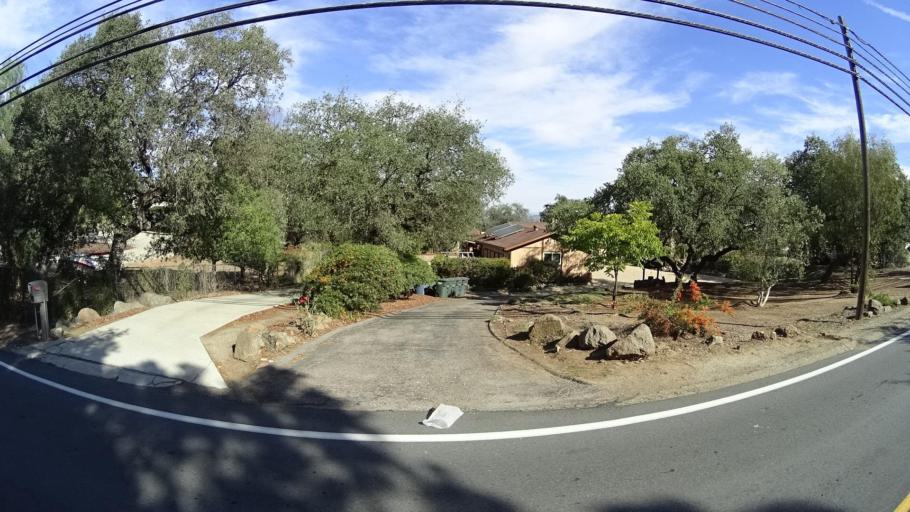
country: US
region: California
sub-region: San Diego County
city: Alpine
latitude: 32.8190
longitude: -116.7915
